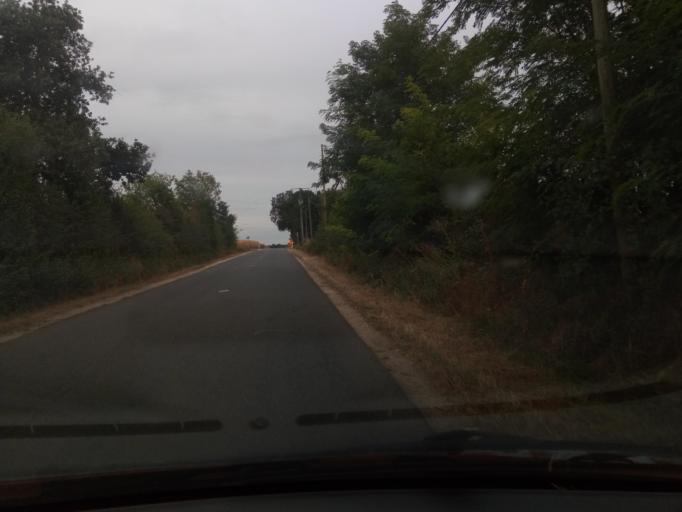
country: FR
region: Poitou-Charentes
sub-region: Departement de la Vienne
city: Saint-Savin
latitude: 46.5483
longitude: 0.7783
